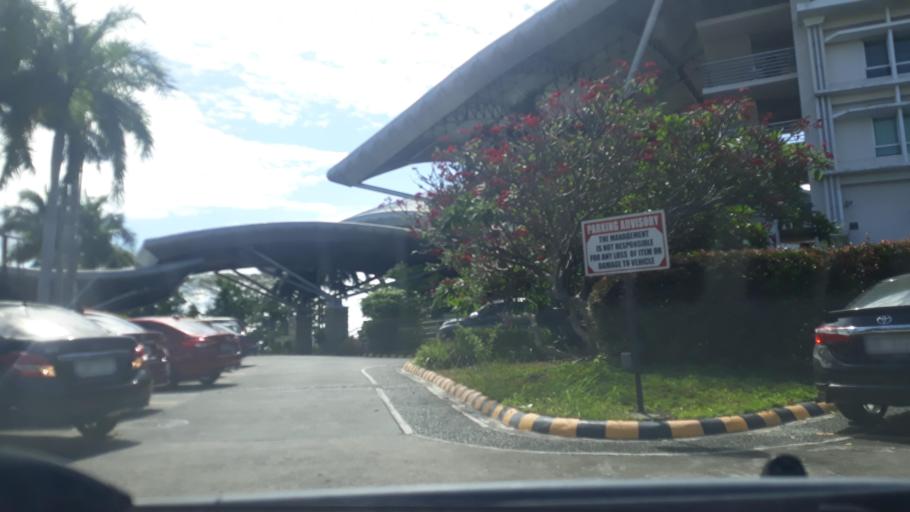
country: PH
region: Calabarzon
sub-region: Province of Cavite
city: Manggahan
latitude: 14.2919
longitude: 120.9150
